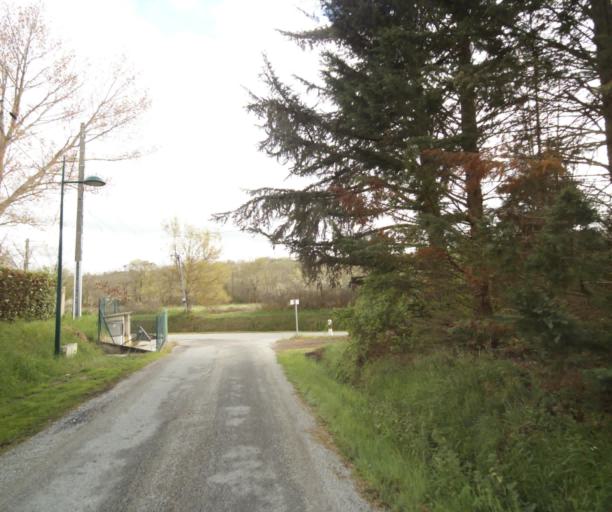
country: FR
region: Midi-Pyrenees
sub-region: Departement de l'Ariege
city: Saverdun
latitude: 43.2197
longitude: 1.5721
